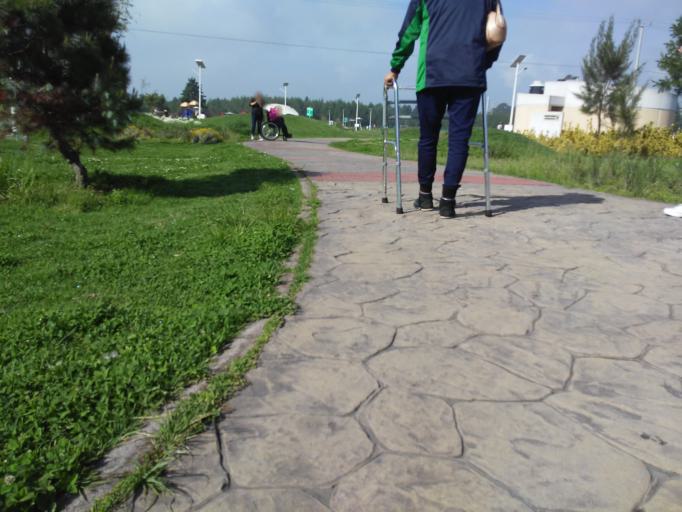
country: MX
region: Mexico
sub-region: Metepec
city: San Salvador Tizatlalli
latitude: 19.2486
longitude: -99.5821
